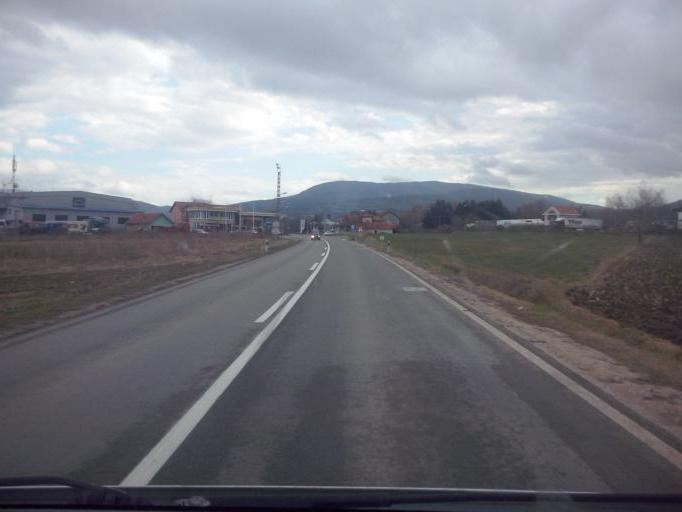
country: RS
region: Central Serbia
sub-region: Pomoravski Okrug
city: Paracin
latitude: 43.8560
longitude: 21.5548
